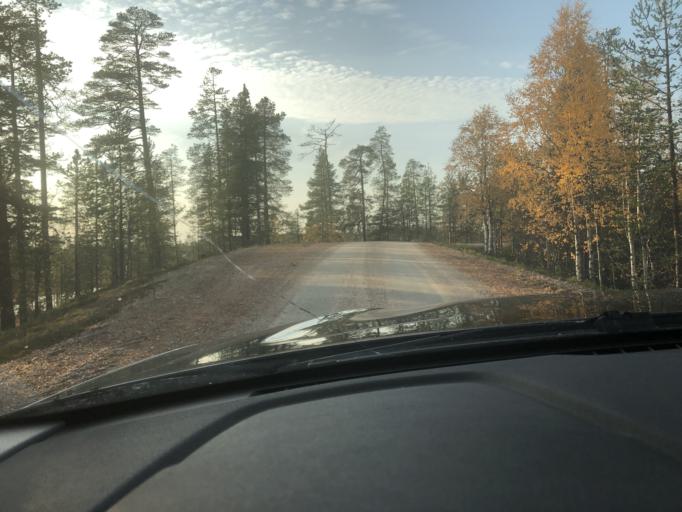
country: FI
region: Northern Ostrobothnia
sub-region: Koillismaa
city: Kuusamo
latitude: 66.5170
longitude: 29.2221
